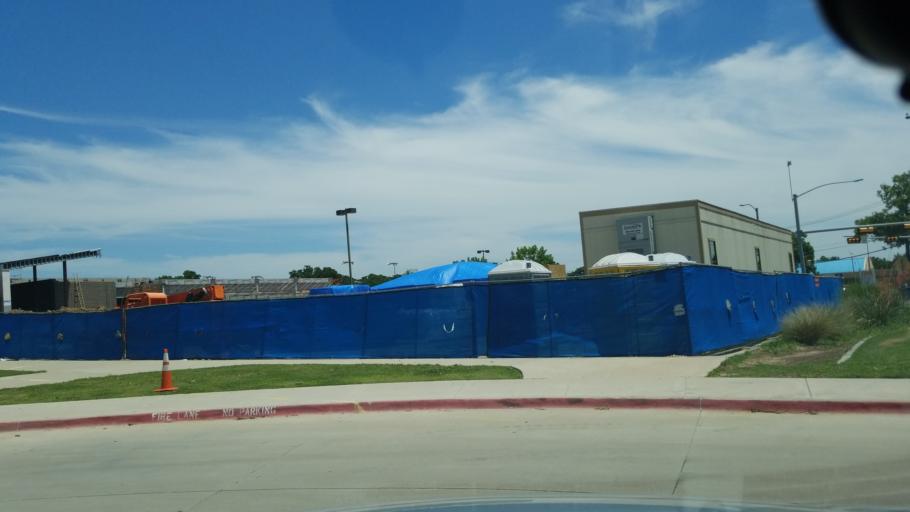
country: US
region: Texas
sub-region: Dallas County
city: Irving
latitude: 32.8243
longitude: -96.9508
